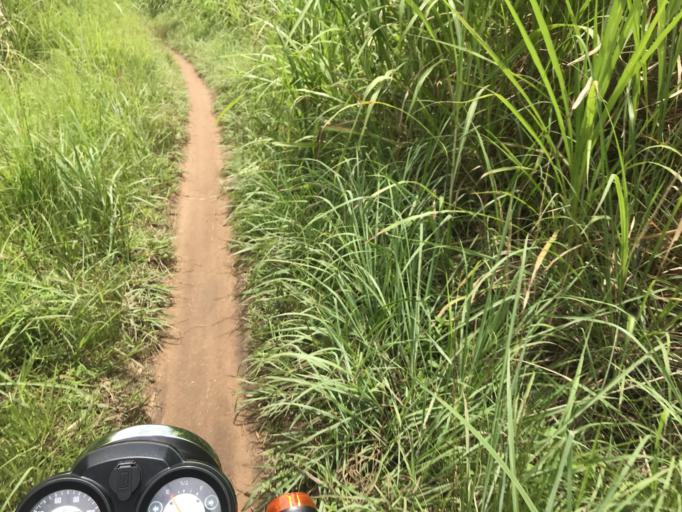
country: GN
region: Nzerekore
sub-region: Prefecture de Guekedou
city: Gueckedou
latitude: 8.4997
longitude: -10.3291
